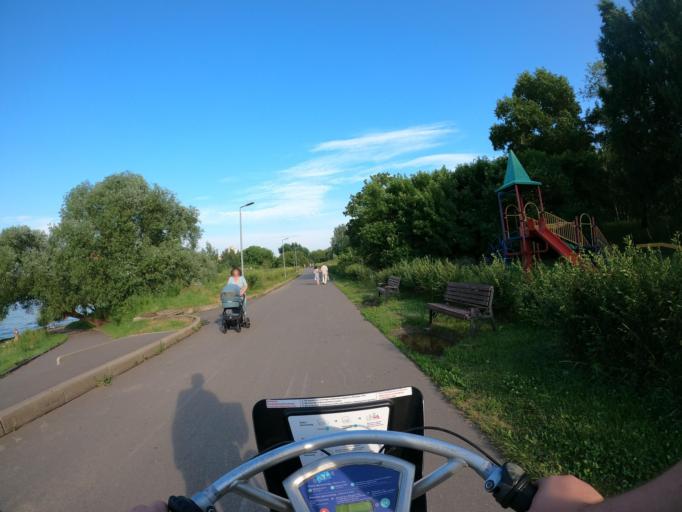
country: RU
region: Moscow
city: Strogino
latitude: 55.8110
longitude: 37.4173
